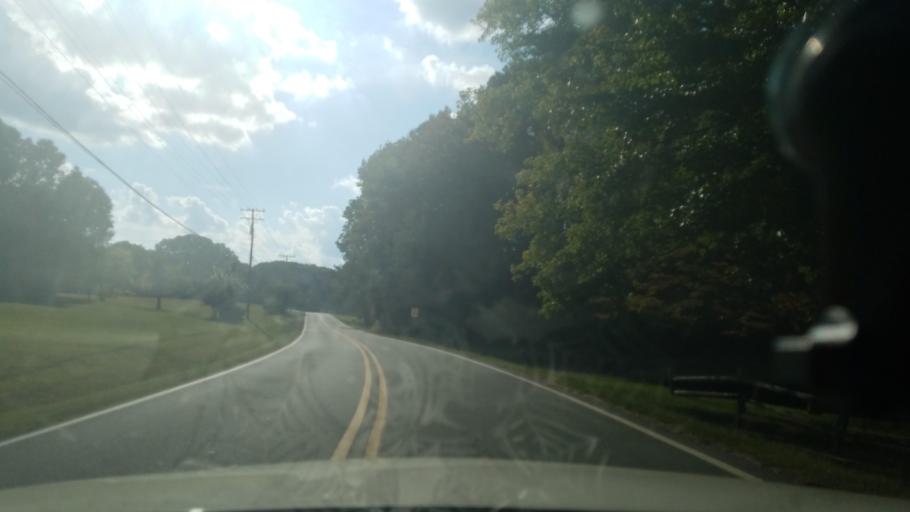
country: US
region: North Carolina
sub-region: Guilford County
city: Pleasant Garden
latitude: 36.0132
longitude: -79.7640
